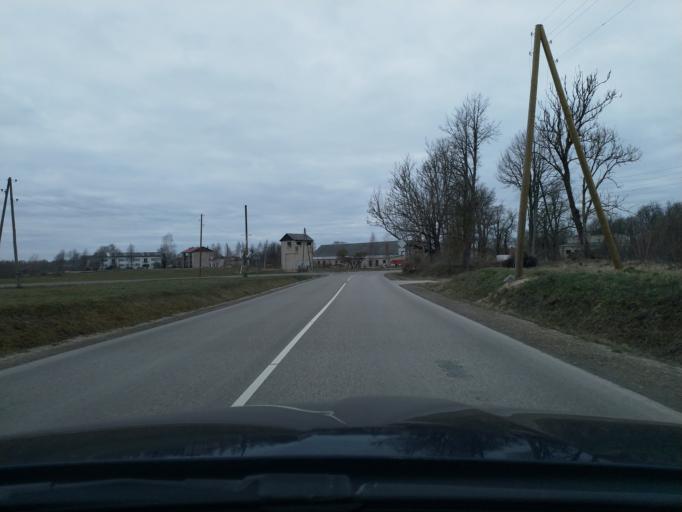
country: LV
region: Talsu Rajons
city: Sabile
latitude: 56.9474
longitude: 22.4006
